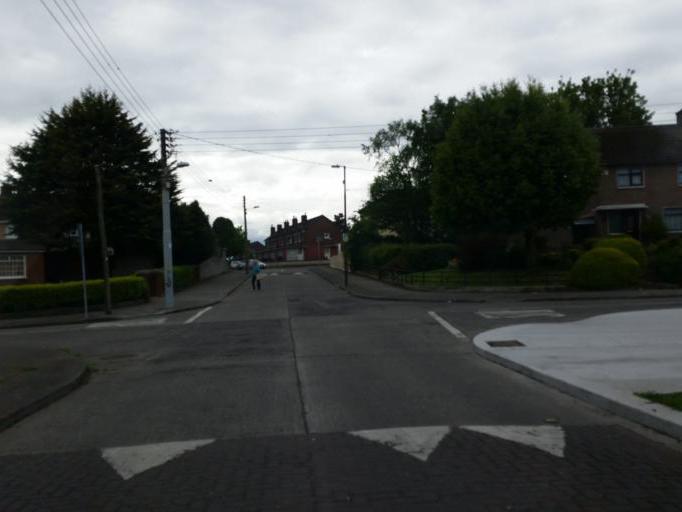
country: IE
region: Leinster
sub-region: Dublin City
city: Finglas
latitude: 53.3922
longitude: -6.3077
